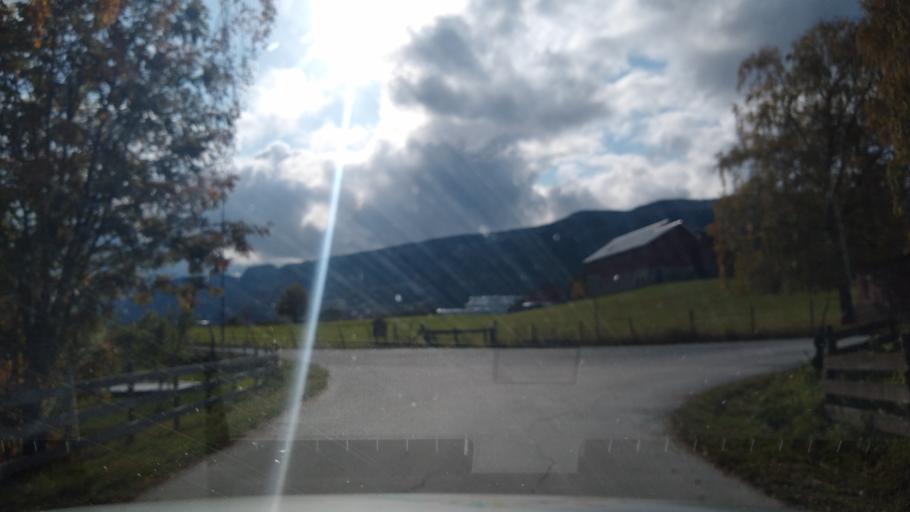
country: NO
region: Oppland
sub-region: Ringebu
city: Ringebu
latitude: 61.5397
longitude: 10.1329
